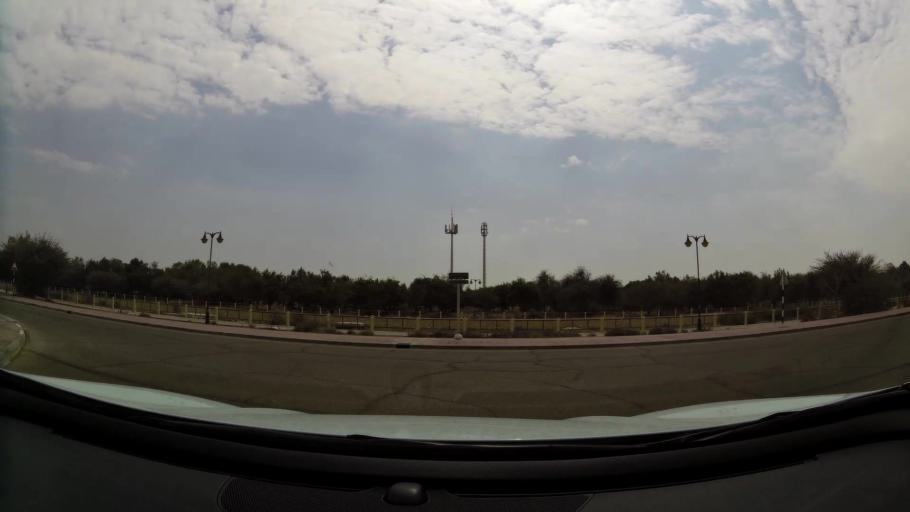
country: AE
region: Abu Dhabi
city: Al Ain
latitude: 24.2112
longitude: 55.7902
